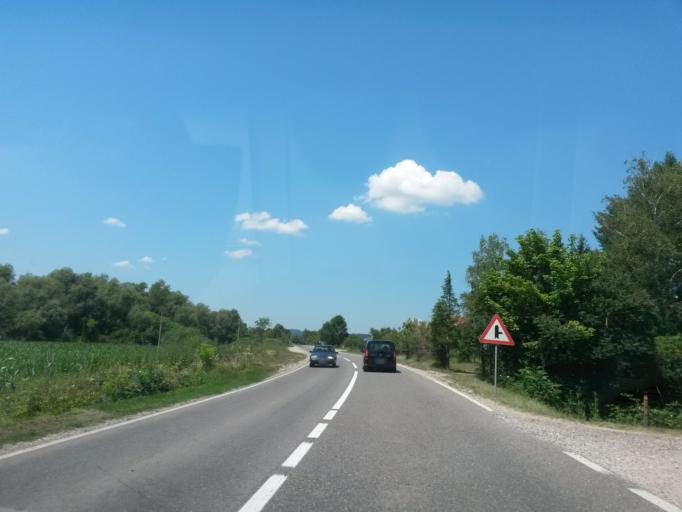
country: BA
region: Federation of Bosnia and Herzegovina
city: Lukavica
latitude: 44.9351
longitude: 18.1458
